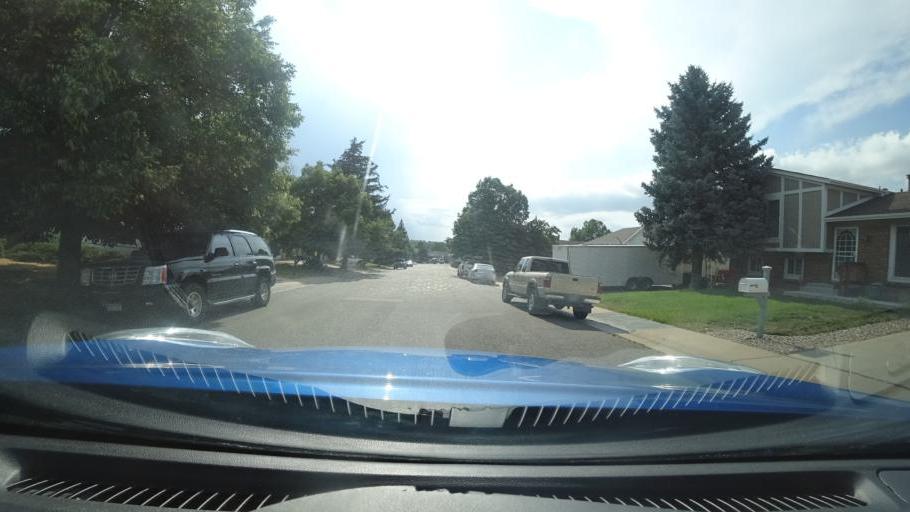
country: US
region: Colorado
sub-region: Adams County
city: Aurora
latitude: 39.6897
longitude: -104.7982
